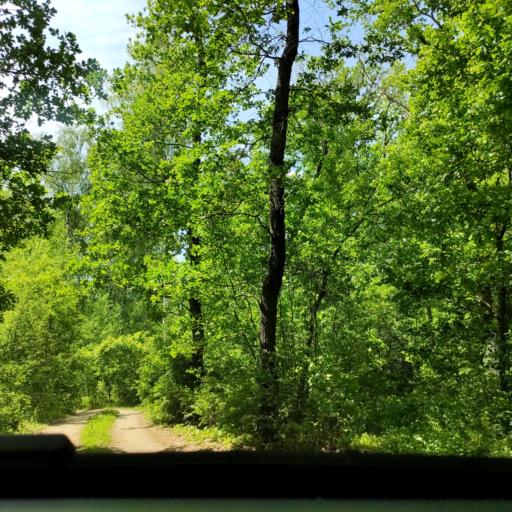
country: RU
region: Voronezj
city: Podgornoye
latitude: 51.8049
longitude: 39.1486
